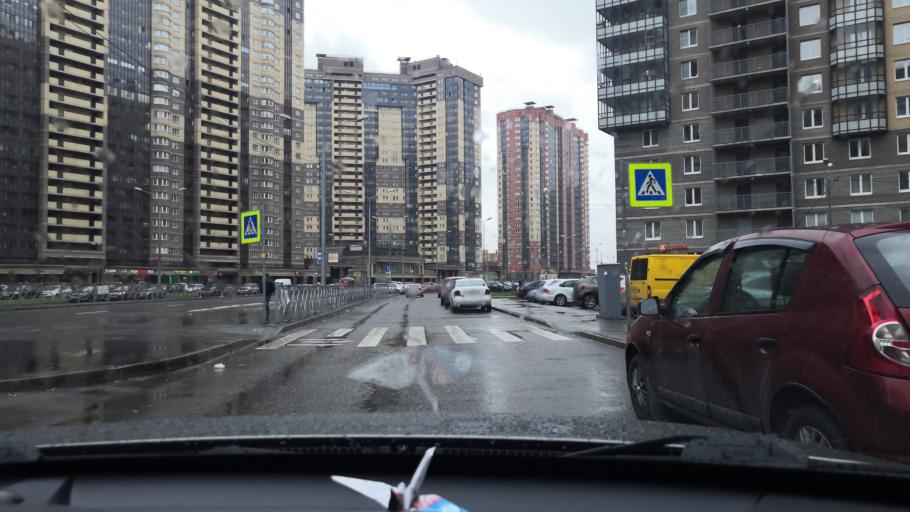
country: RU
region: Leningrad
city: Parnas
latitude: 60.0795
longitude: 30.3427
